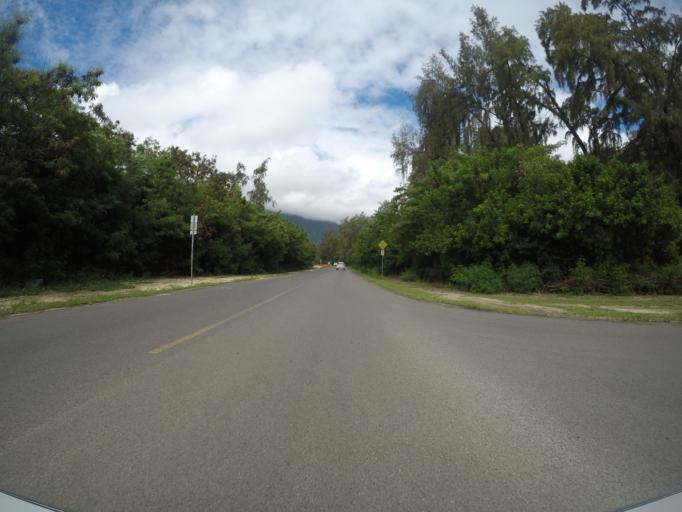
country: US
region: Hawaii
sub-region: Honolulu County
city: Waimanalo Beach
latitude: 21.3443
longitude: -157.7050
